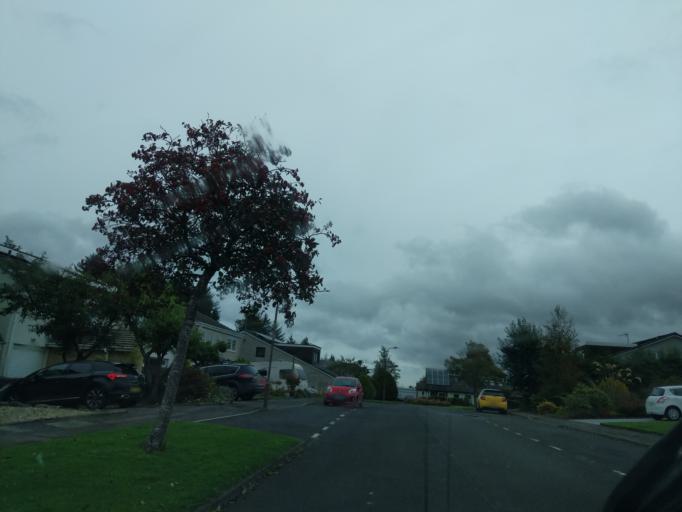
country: GB
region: Scotland
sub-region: Edinburgh
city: Balerno
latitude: 55.8793
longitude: -3.3479
